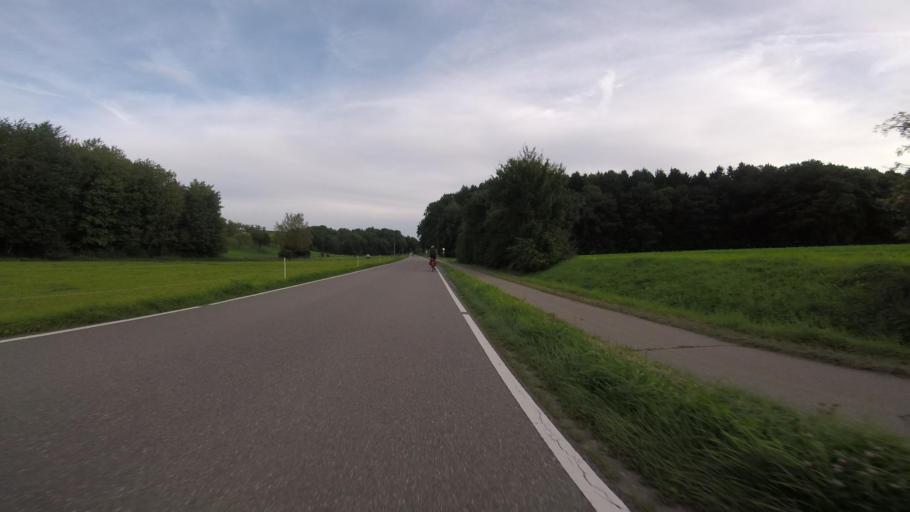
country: DE
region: Baden-Wuerttemberg
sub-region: Regierungsbezirk Stuttgart
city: Aspach
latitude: 48.9853
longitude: 9.3954
